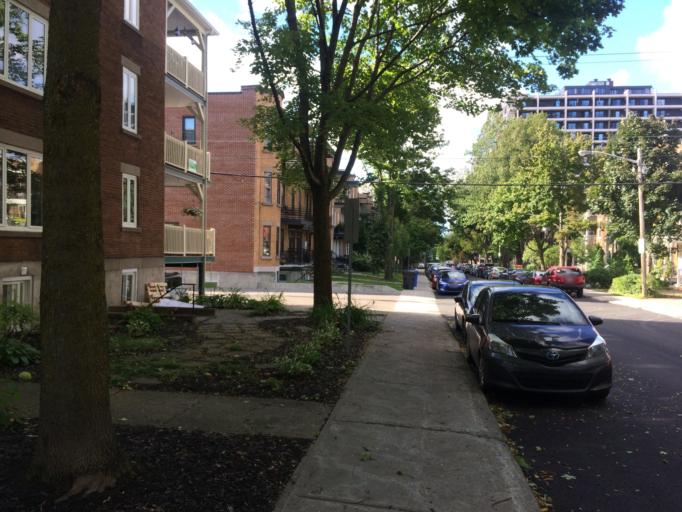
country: CA
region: Quebec
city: Quebec
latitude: 46.8012
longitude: -71.2323
